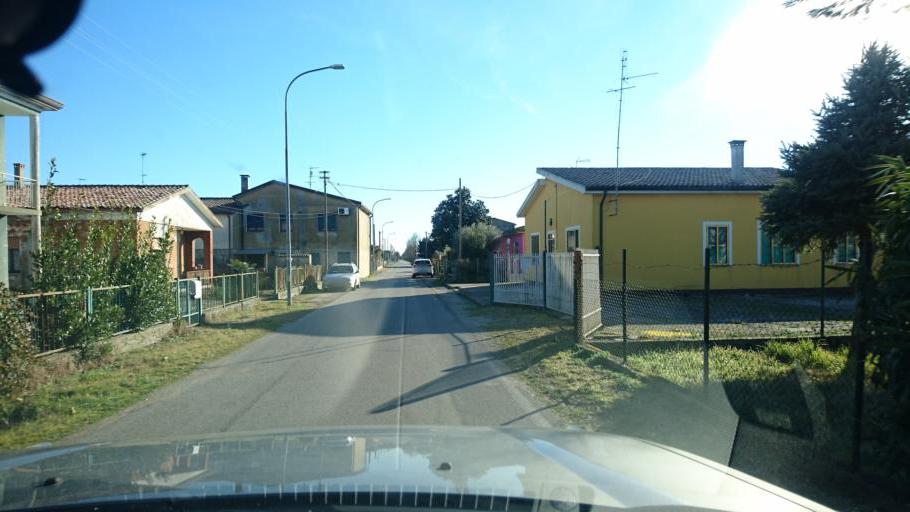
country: IT
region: Veneto
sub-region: Provincia di Rovigo
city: Corbola
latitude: 45.0158
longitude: 12.1153
